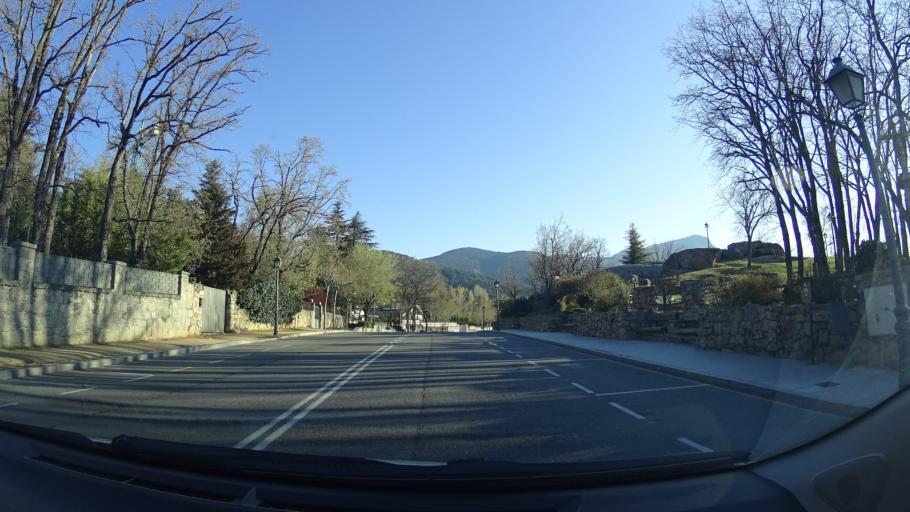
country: ES
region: Madrid
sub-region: Provincia de Madrid
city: Navacerrada
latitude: 40.7253
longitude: -4.0195
